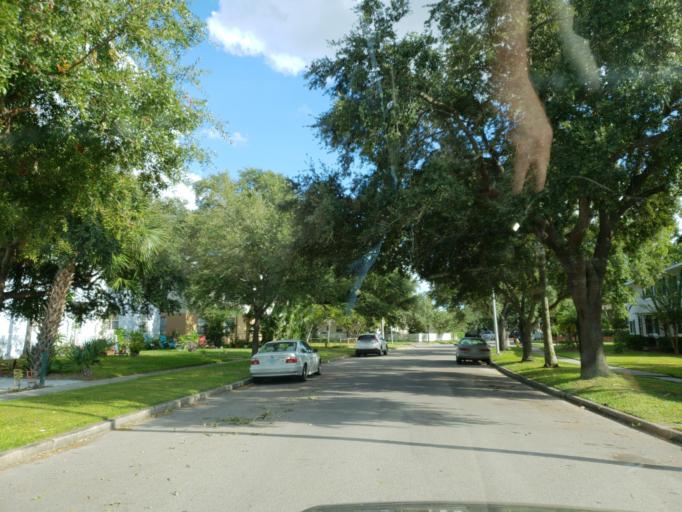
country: US
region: Florida
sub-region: Hillsborough County
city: Tampa
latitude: 27.9278
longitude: -82.4552
